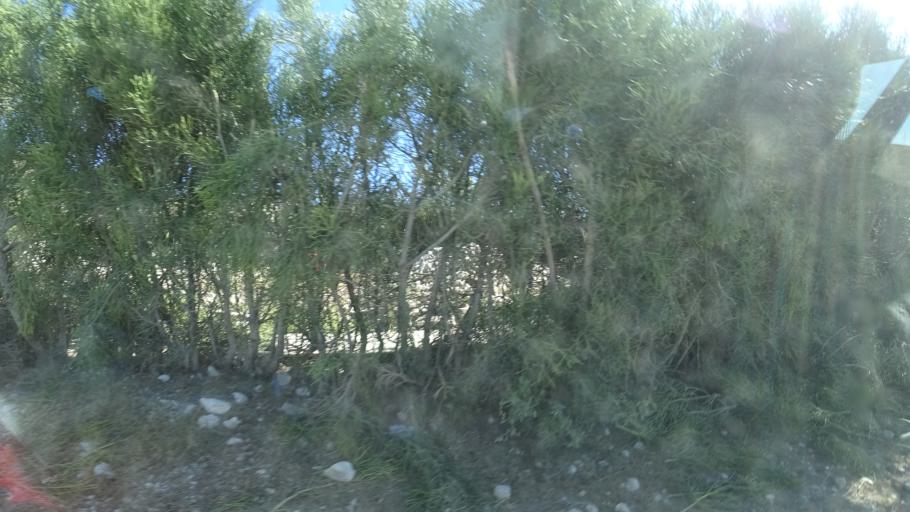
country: HT
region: Ouest
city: Croix des Bouquets
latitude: 18.6749
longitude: -72.2399
